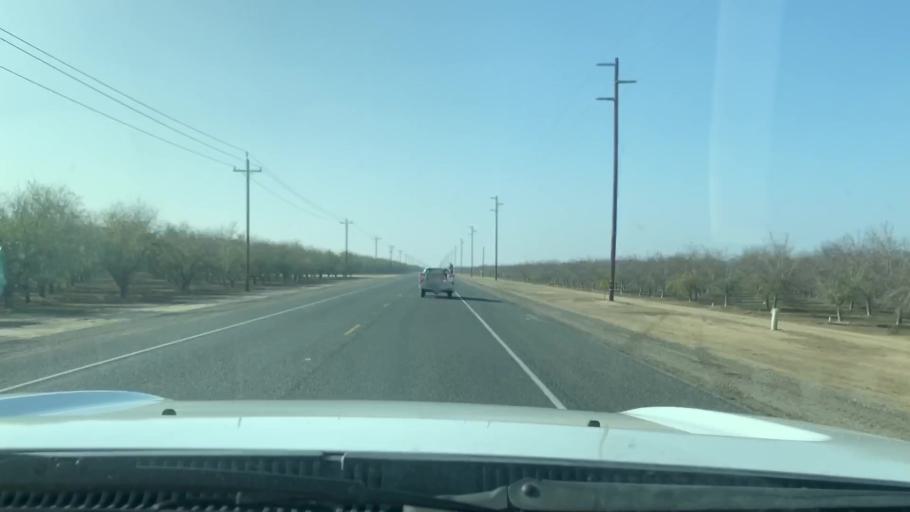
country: US
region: California
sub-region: Kern County
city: Wasco
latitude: 35.6012
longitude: -119.4579
